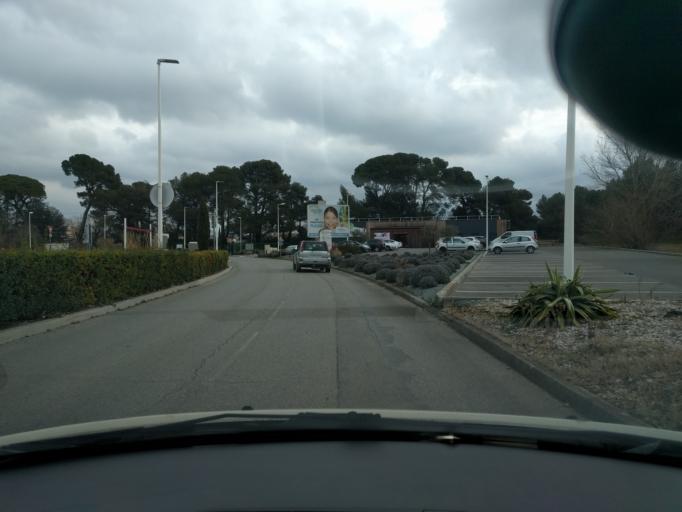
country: FR
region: Provence-Alpes-Cote d'Azur
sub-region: Departement des Bouches-du-Rhone
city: Bouc-Bel-Air
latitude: 43.4294
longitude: 5.4019
